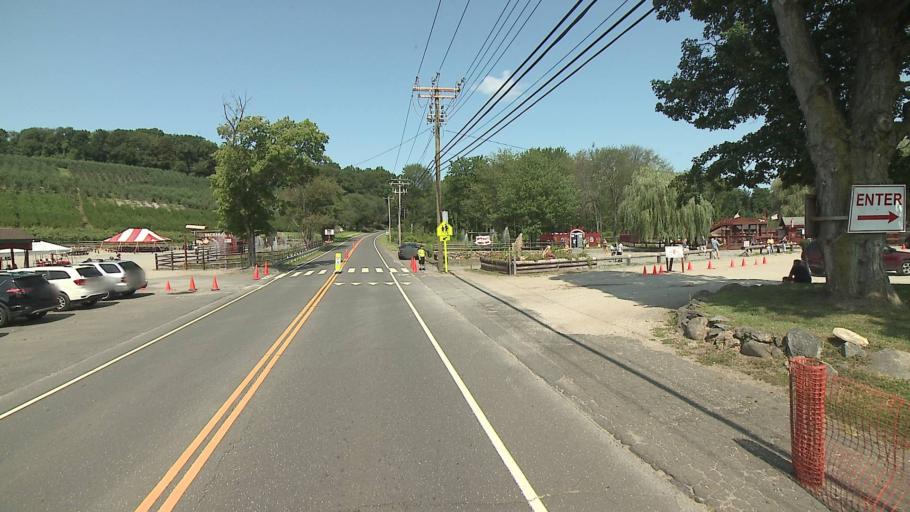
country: US
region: Connecticut
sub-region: Fairfield County
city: Trumbull
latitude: 41.2499
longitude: -73.2791
